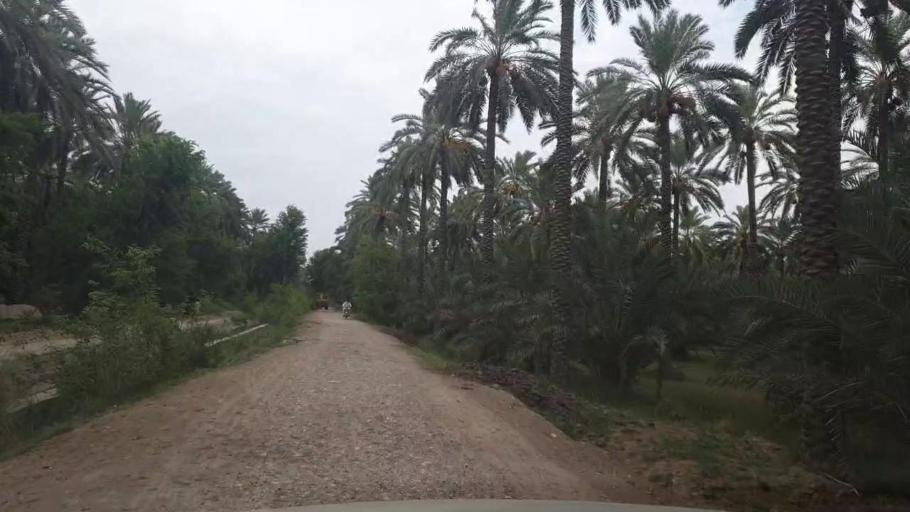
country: PK
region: Sindh
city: Sukkur
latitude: 27.6331
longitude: 68.8202
